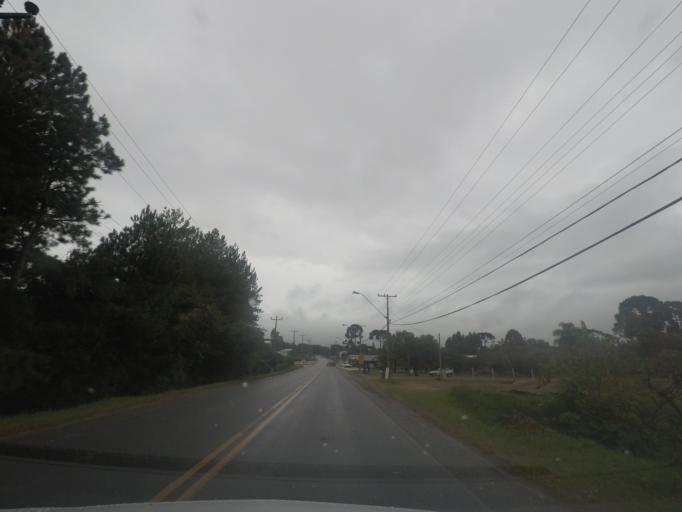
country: BR
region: Parana
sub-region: Campina Grande Do Sul
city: Campina Grande do Sul
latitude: -25.3172
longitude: -49.0750
